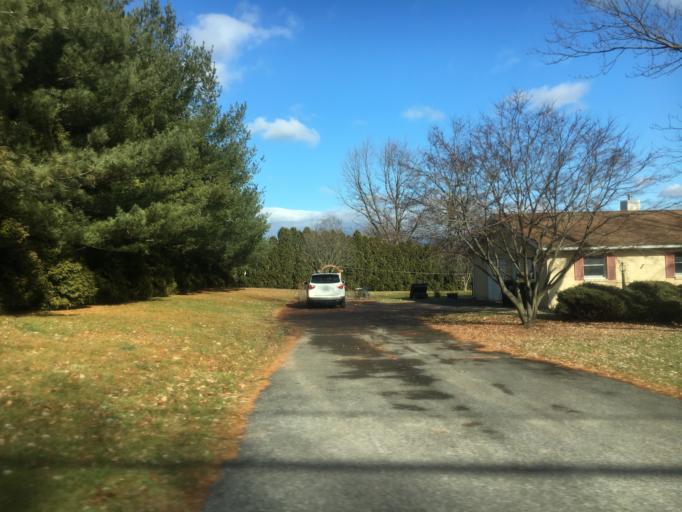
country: US
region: Pennsylvania
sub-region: Lehigh County
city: Egypt
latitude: 40.6906
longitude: -75.5547
